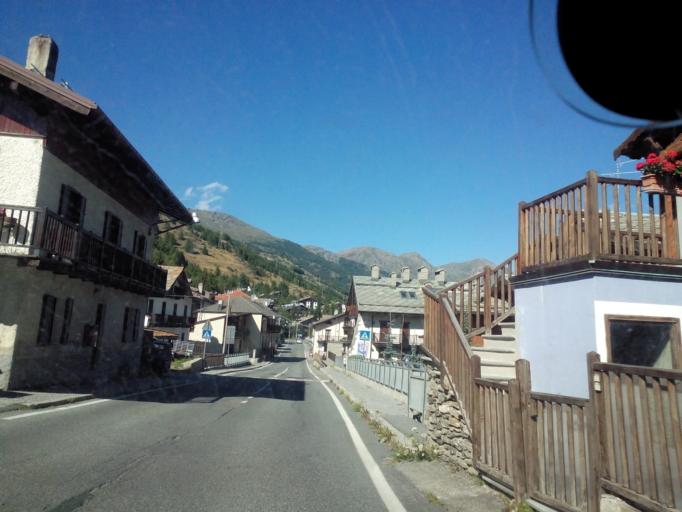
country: IT
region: Piedmont
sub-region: Provincia di Torino
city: Pragelato-Rua
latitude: 45.0079
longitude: 6.9338
